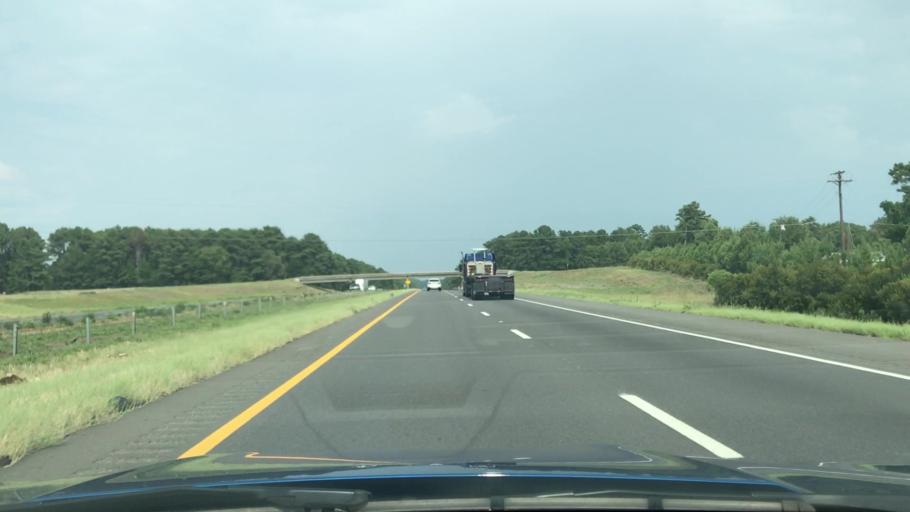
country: US
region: Texas
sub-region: Harrison County
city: Hallsville
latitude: 32.4661
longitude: -94.6249
